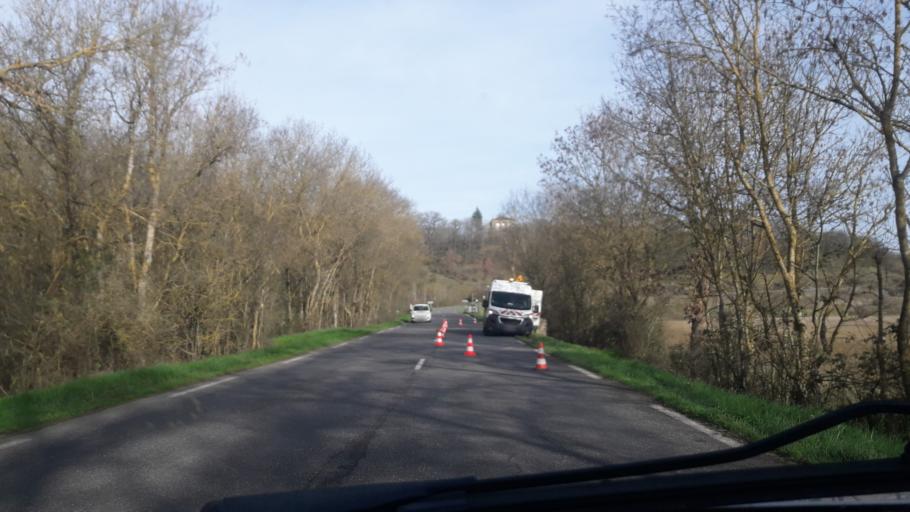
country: FR
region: Midi-Pyrenees
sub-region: Departement du Gers
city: Gimont
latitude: 43.7306
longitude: 0.9010
